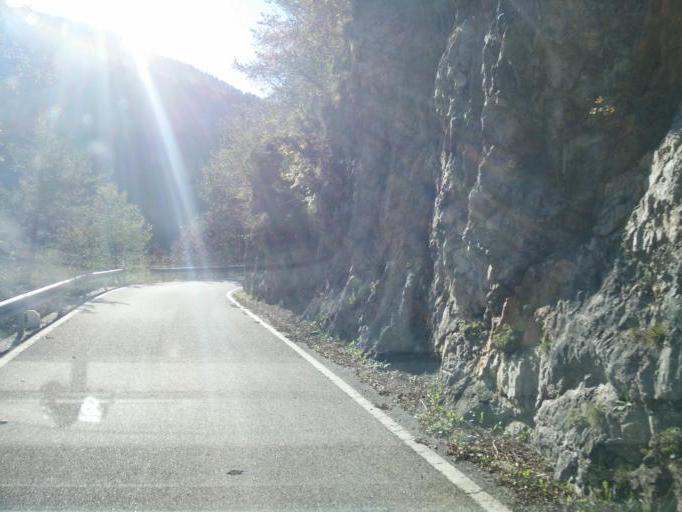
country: IT
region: Lombardy
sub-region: Provincia di Brescia
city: Valvestino
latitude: 45.7508
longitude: 10.5712
